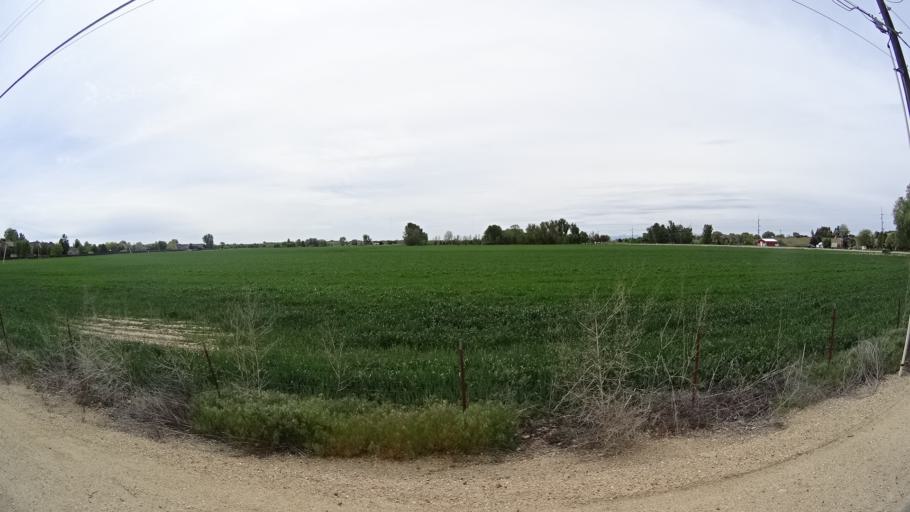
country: US
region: Idaho
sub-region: Ada County
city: Kuna
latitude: 43.5321
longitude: -116.3326
